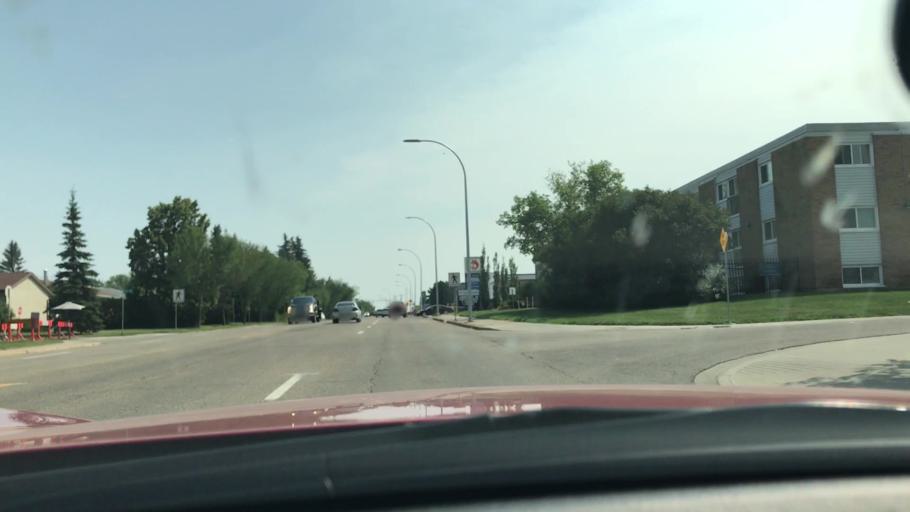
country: CA
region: Alberta
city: Edmonton
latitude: 53.5411
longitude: -113.4287
